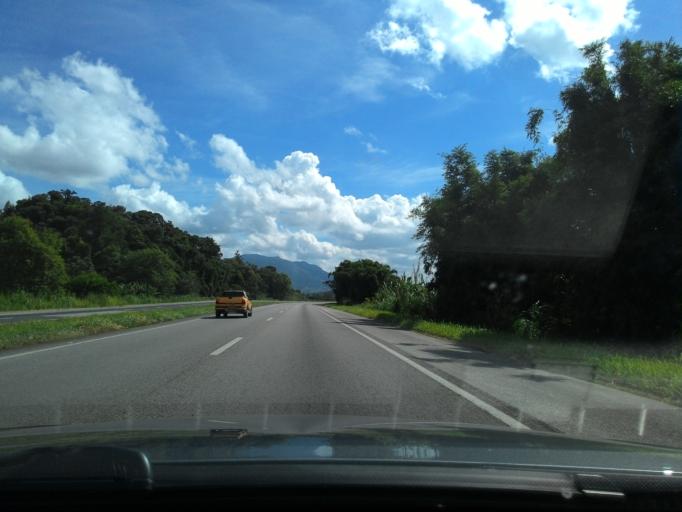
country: BR
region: Sao Paulo
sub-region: Jacupiranga
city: Jacupiranga
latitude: -24.7206
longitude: -48.0416
